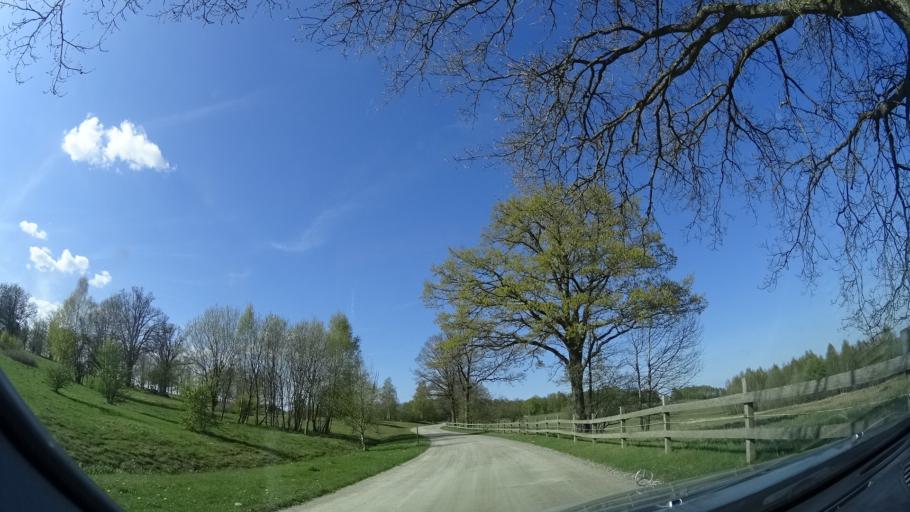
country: SE
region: Skane
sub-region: Hassleholms Kommun
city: Tormestorp
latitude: 56.1085
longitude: 13.6963
